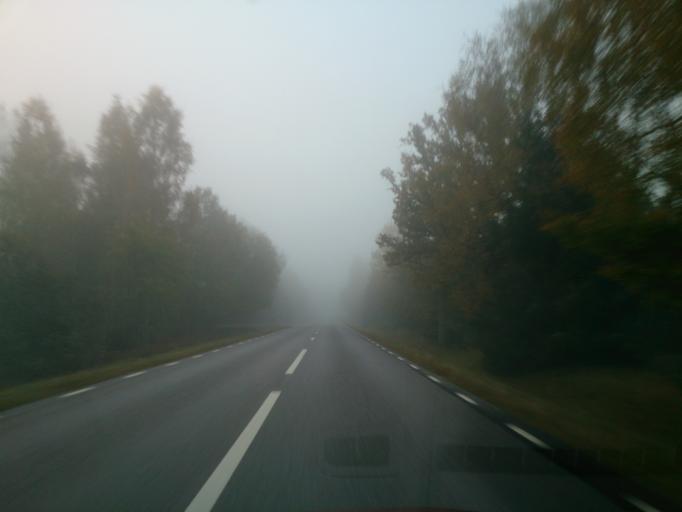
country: SE
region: OEstergoetland
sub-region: Atvidabergs Kommun
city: Atvidaberg
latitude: 58.1206
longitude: 15.9541
